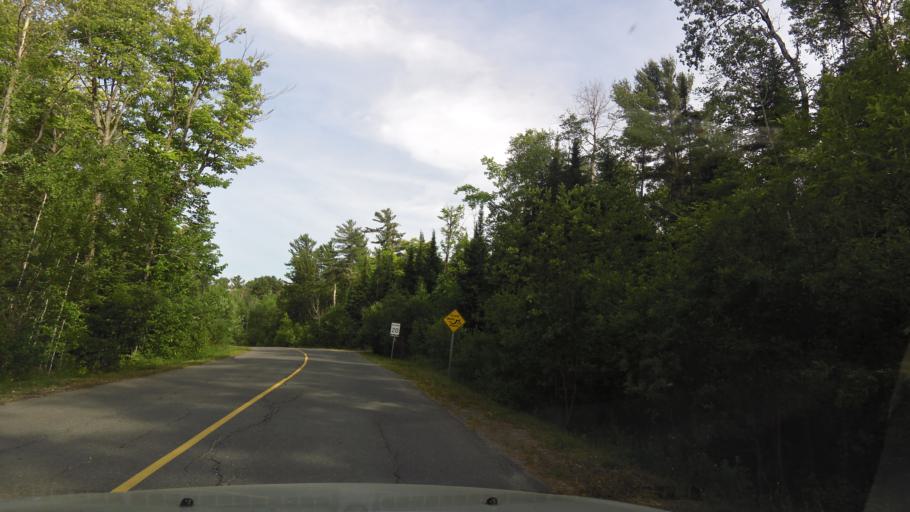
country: CA
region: Ontario
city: Greater Sudbury
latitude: 46.0153
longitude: -80.5838
